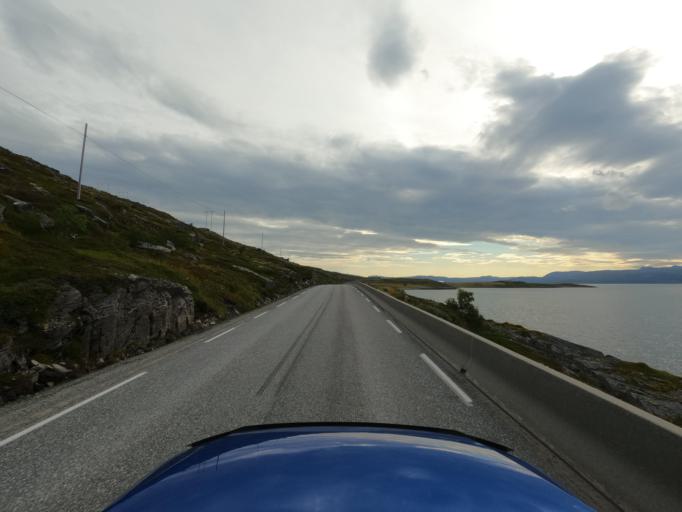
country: NO
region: Finnmark Fylke
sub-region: Hammerfest
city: Rypefjord
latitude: 70.5735
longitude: 23.6937
